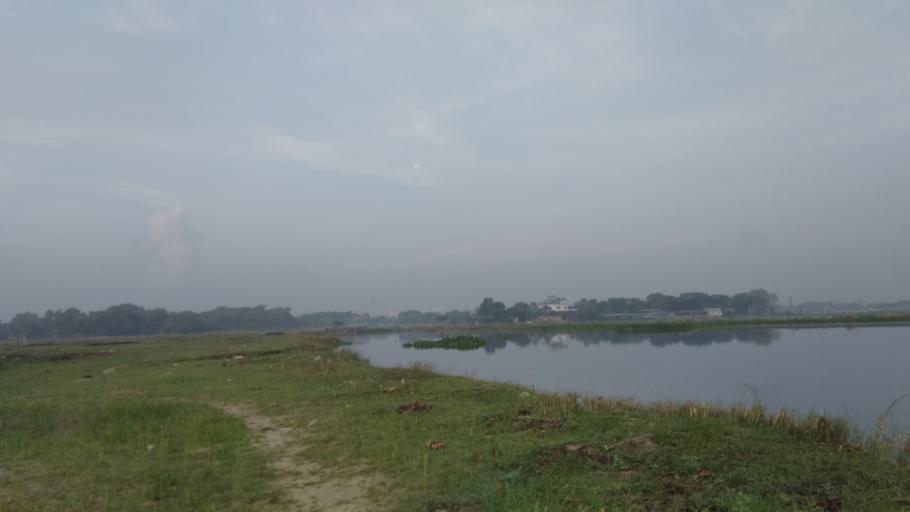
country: BD
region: Dhaka
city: Tungi
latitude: 23.8510
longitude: 90.4466
